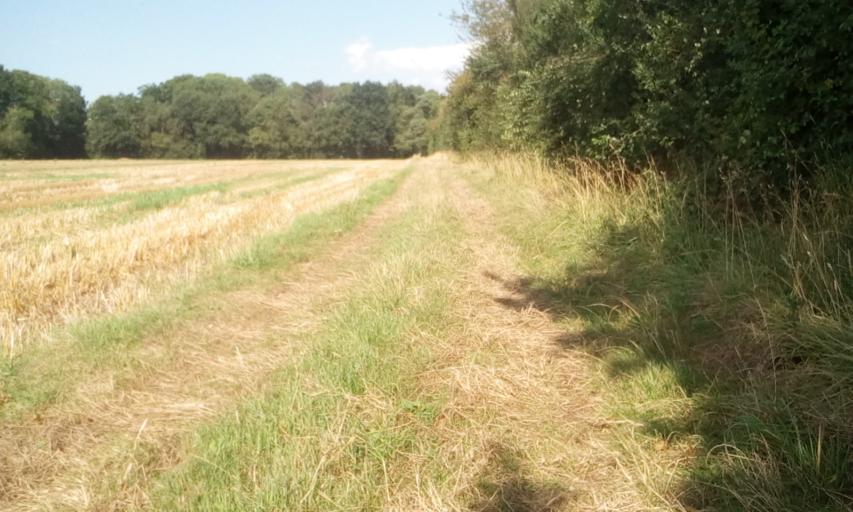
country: FR
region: Lower Normandy
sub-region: Departement du Calvados
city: Argences
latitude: 49.1399
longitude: -0.1117
